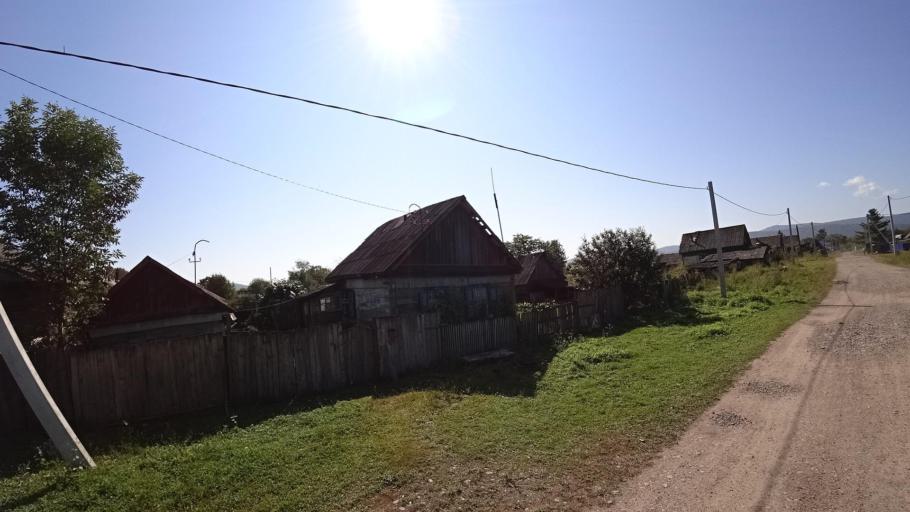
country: RU
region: Jewish Autonomous Oblast
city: Bira
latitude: 48.9995
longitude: 132.4508
